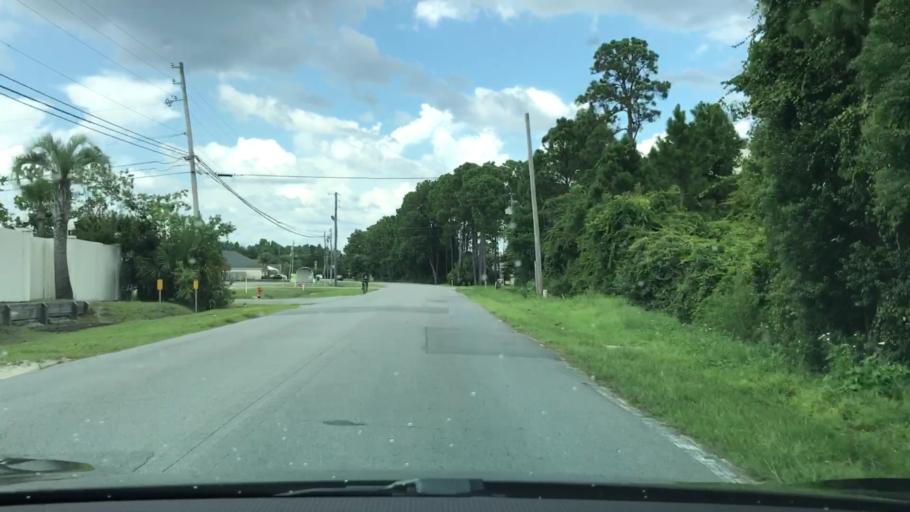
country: US
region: Florida
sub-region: Bay County
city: Panama City Beach
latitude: 30.1851
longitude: -85.7865
